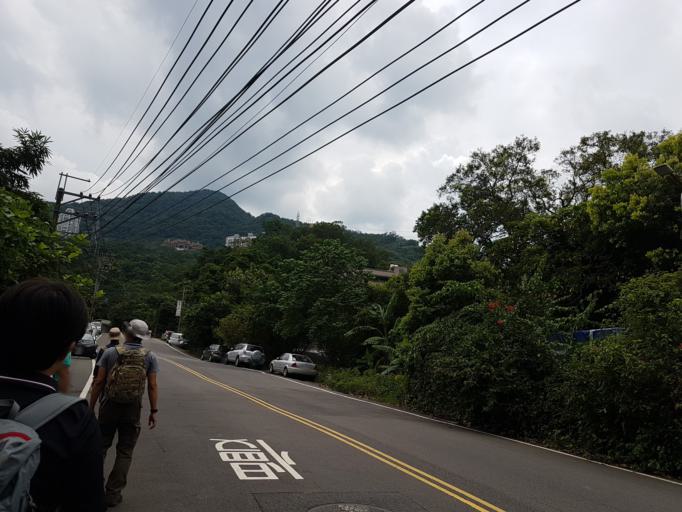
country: TW
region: Taiwan
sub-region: Keelung
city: Keelung
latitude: 25.0587
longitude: 121.6607
